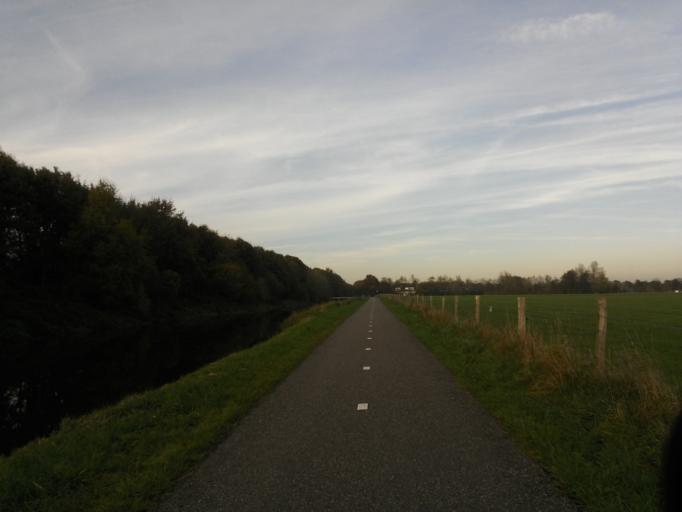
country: NL
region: Utrecht
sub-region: Gemeente Leusden
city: Leusden
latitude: 52.1242
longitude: 5.4463
